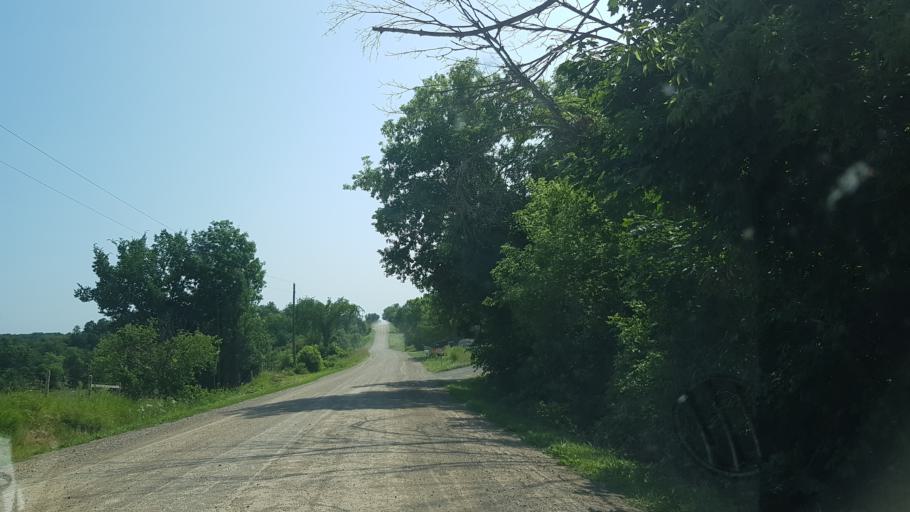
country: CA
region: Ontario
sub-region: Oxford County
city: Woodstock
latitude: 42.9461
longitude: -80.6733
